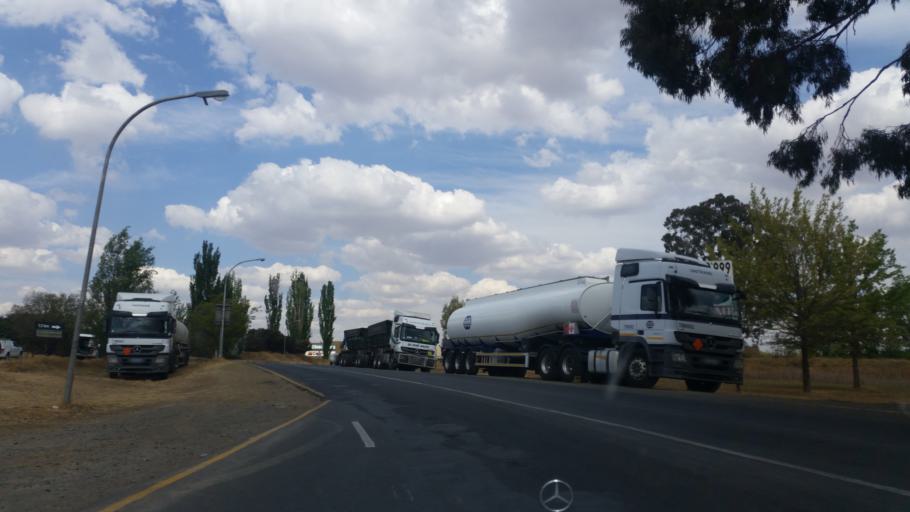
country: ZA
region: Orange Free State
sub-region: Thabo Mofutsanyana District Municipality
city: Bethlehem
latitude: -28.2399
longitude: 28.3220
